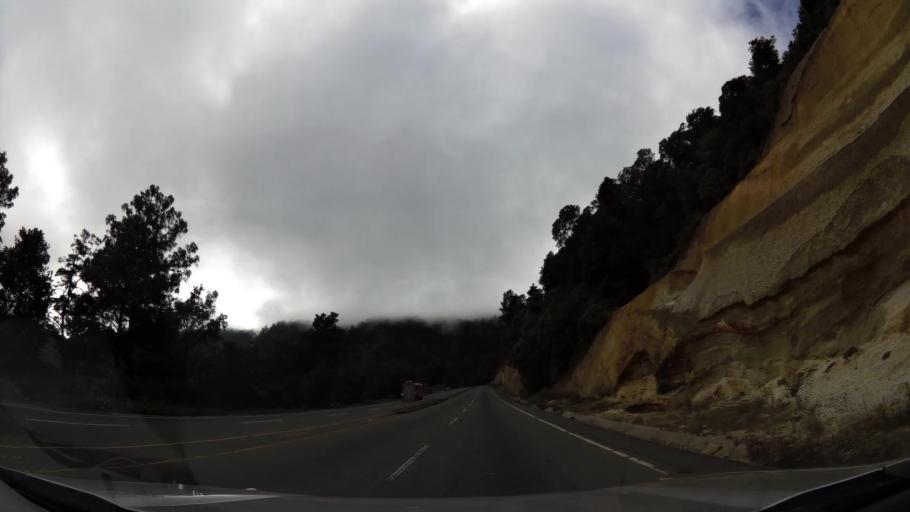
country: GT
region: Quetzaltenango
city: Cantel
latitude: 14.8458
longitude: -91.4055
